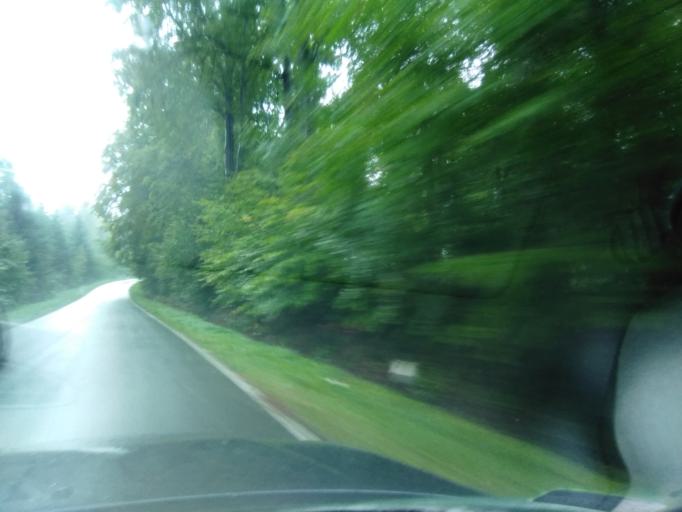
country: PL
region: Subcarpathian Voivodeship
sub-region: Powiat ropczycko-sedziszowski
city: Niedzwiada
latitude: 50.0516
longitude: 21.5344
